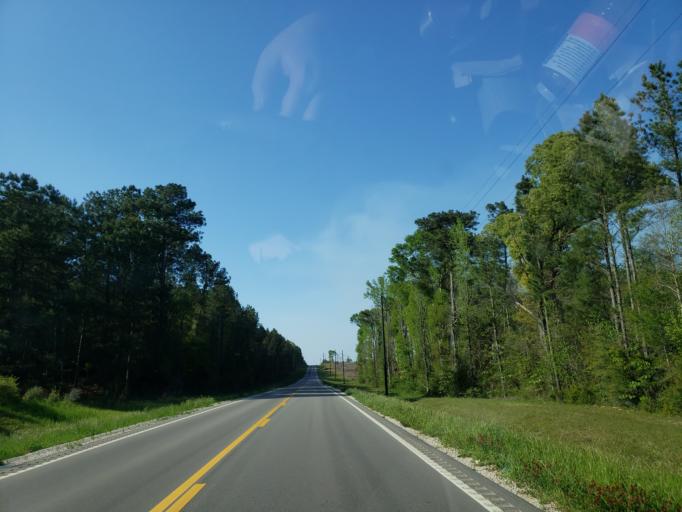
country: US
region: Mississippi
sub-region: Perry County
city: Richton
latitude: 31.2877
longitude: -88.9233
